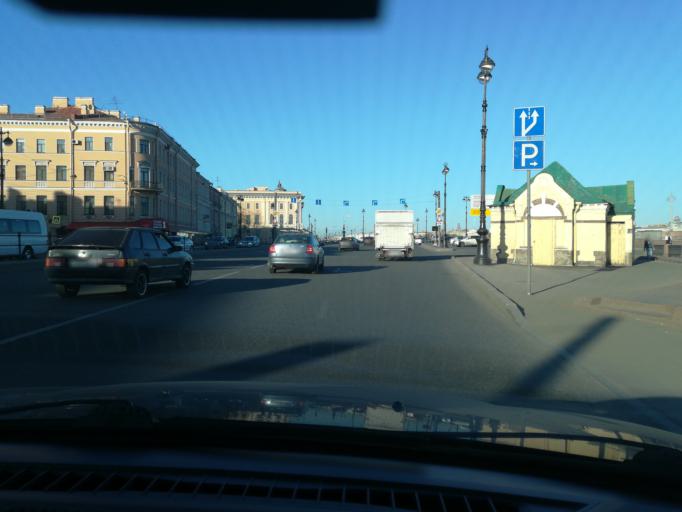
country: RU
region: St.-Petersburg
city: Admiralteisky
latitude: 59.9361
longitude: 30.2856
